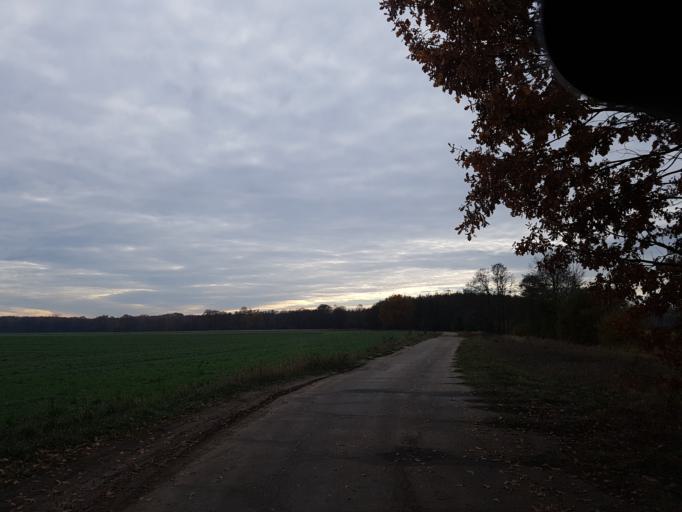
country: DE
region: Brandenburg
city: Treuenbrietzen
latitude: 52.1030
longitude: 12.9224
